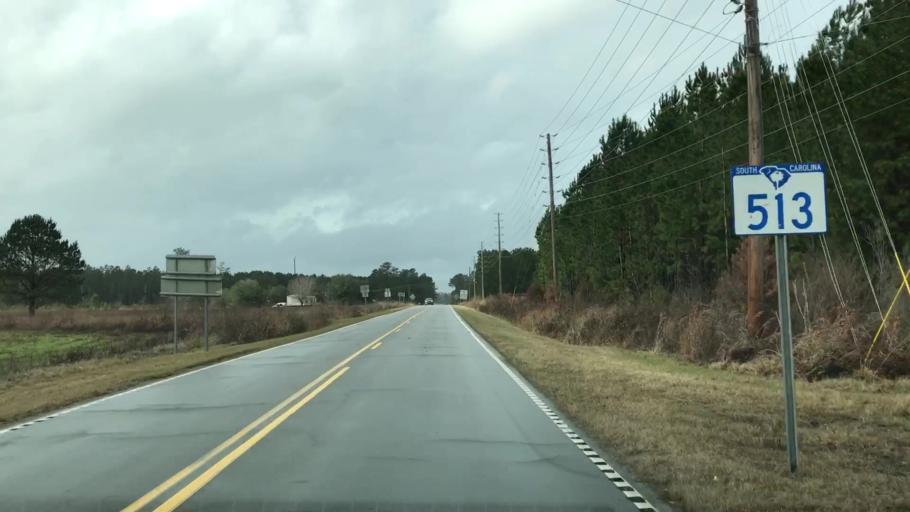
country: US
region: South Carolina
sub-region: Florence County
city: Johnsonville
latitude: 33.6706
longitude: -79.3181
